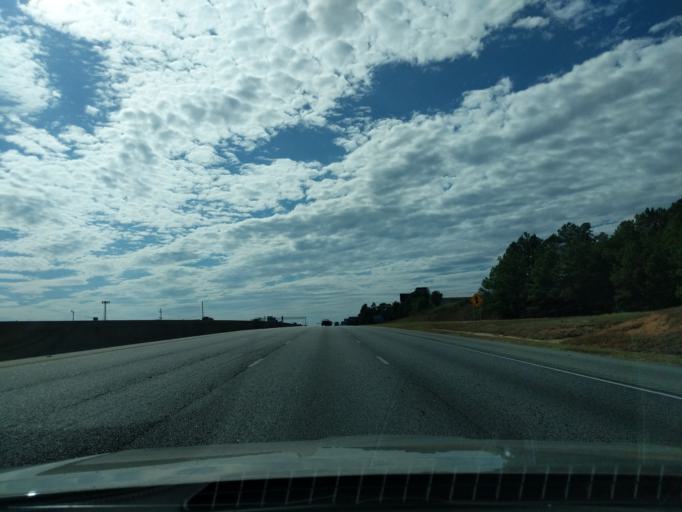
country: US
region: Georgia
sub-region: Columbia County
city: Martinez
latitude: 33.4874
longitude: -82.1105
